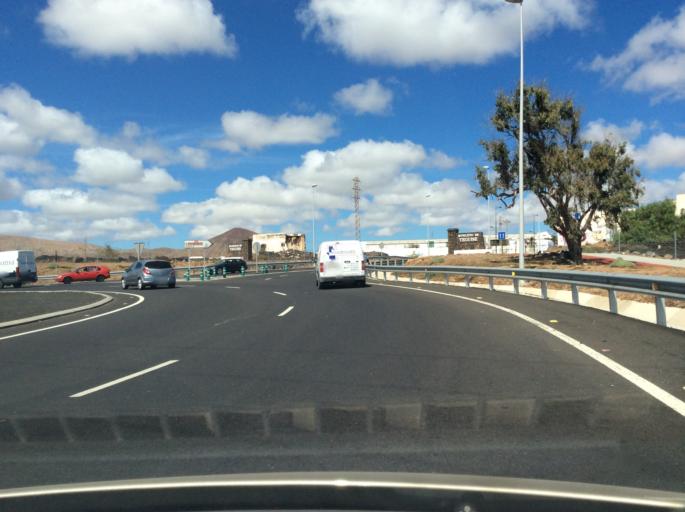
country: ES
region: Canary Islands
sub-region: Provincia de Las Palmas
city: Arrecife
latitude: 28.9819
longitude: -13.5441
